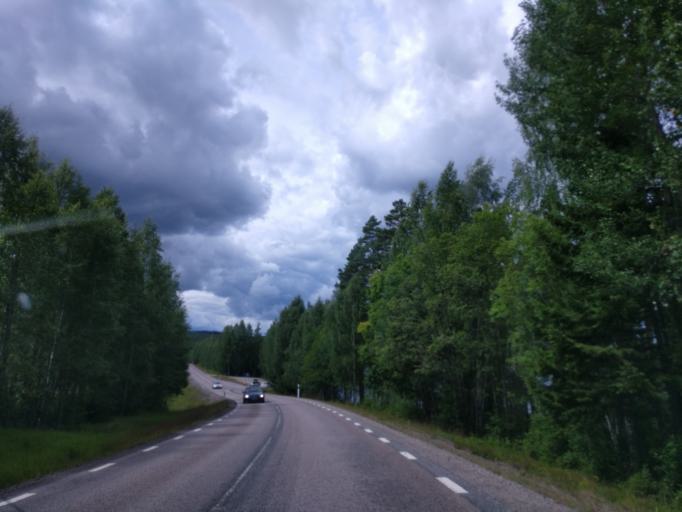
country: SE
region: Vaermland
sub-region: Hagfors Kommun
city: Ekshaerad
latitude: 60.1866
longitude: 13.3355
